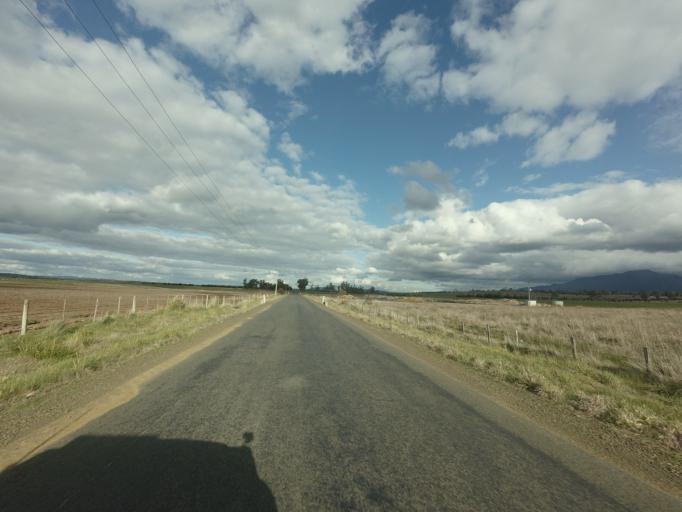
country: AU
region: Tasmania
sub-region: Northern Midlands
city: Longford
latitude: -41.8121
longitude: 147.1893
